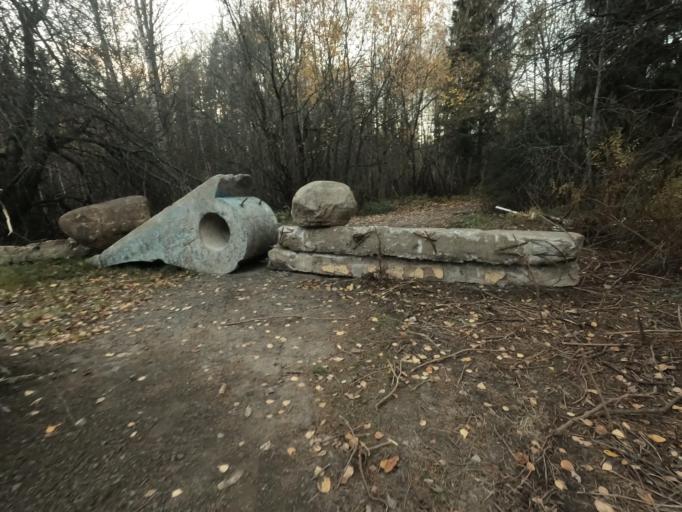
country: RU
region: St.-Petersburg
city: Repino
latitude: 60.1948
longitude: 29.8553
